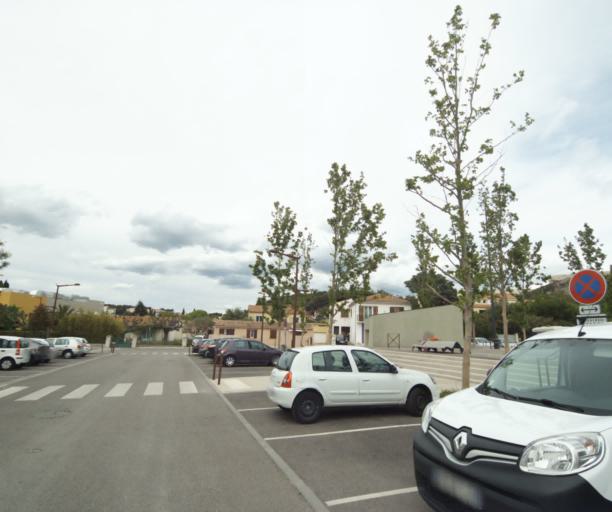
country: FR
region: Provence-Alpes-Cote d'Azur
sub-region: Departement des Bouches-du-Rhone
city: Rognac
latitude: 43.4886
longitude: 5.2325
